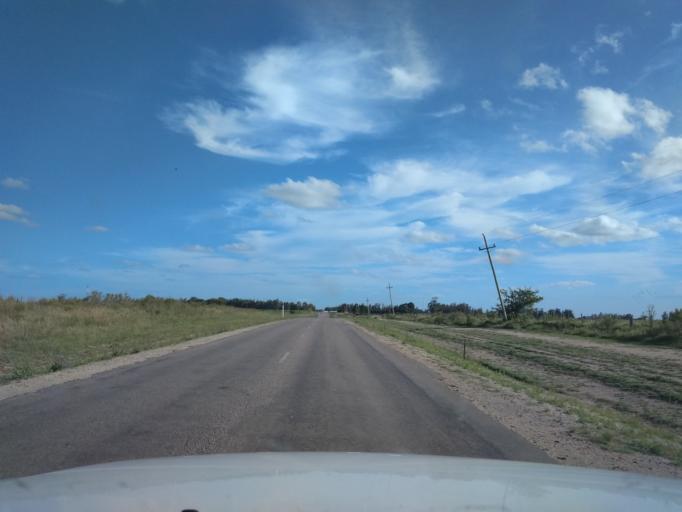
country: UY
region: Canelones
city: San Ramon
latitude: -34.2331
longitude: -55.9280
